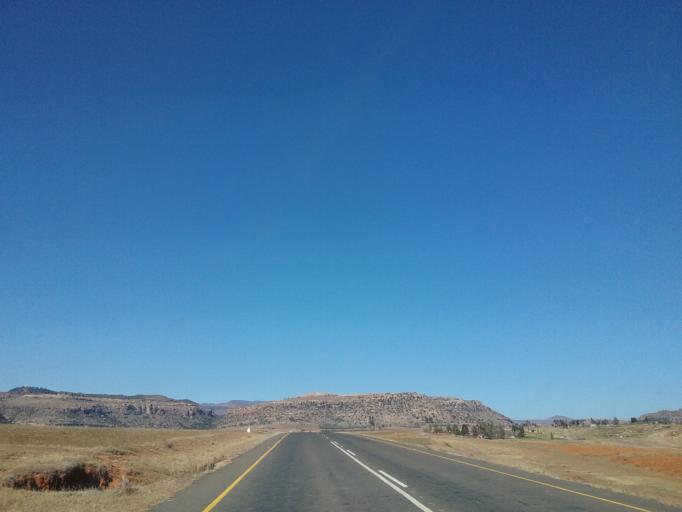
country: LS
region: Maseru
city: Nako
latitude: -29.4767
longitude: 27.6408
